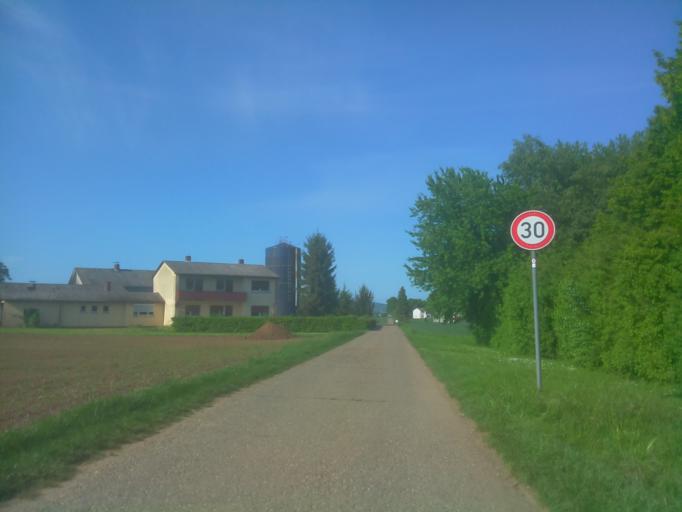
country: DE
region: Baden-Wuerttemberg
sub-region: Karlsruhe Region
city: Ladenburg
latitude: 49.4845
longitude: 8.6175
